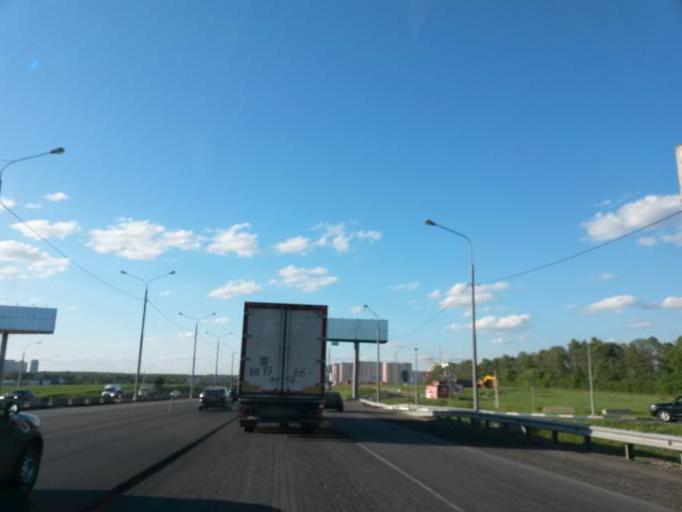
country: RU
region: Moskovskaya
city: Shcherbinka
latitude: 55.5202
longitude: 37.6091
